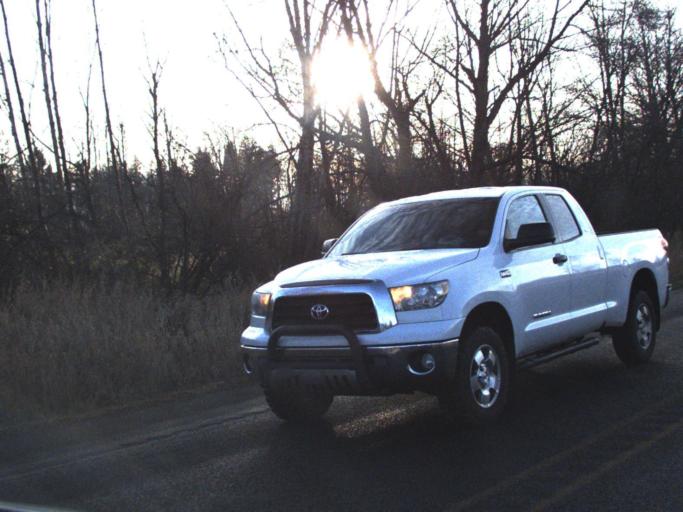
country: US
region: Washington
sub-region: Skagit County
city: Sedro-Woolley
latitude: 48.5267
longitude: -122.1864
